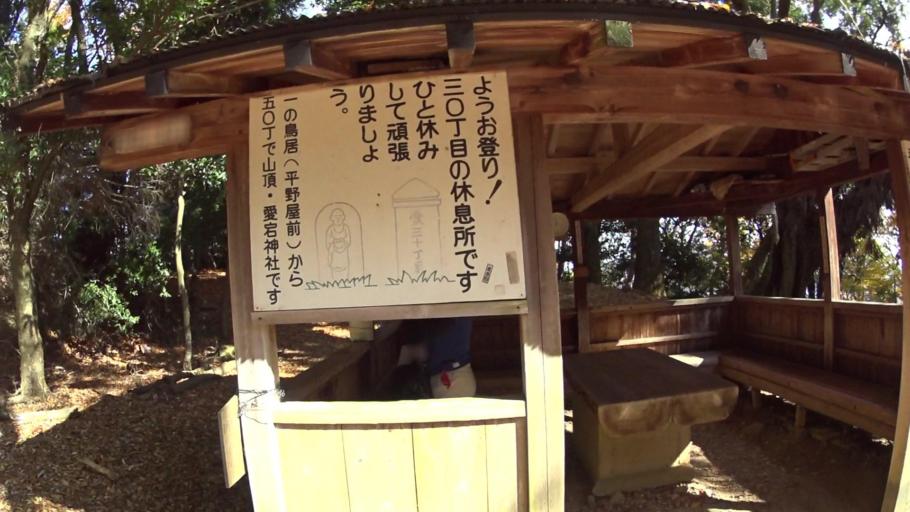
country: JP
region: Kyoto
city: Kameoka
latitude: 35.0474
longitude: 135.6463
